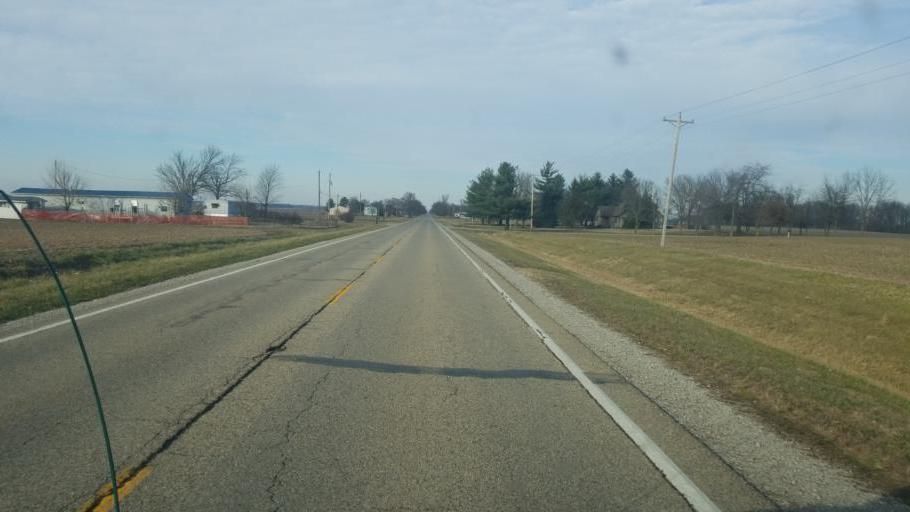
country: US
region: Illinois
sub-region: Lawrence County
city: Bridgeport
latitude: 38.5782
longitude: -87.6945
